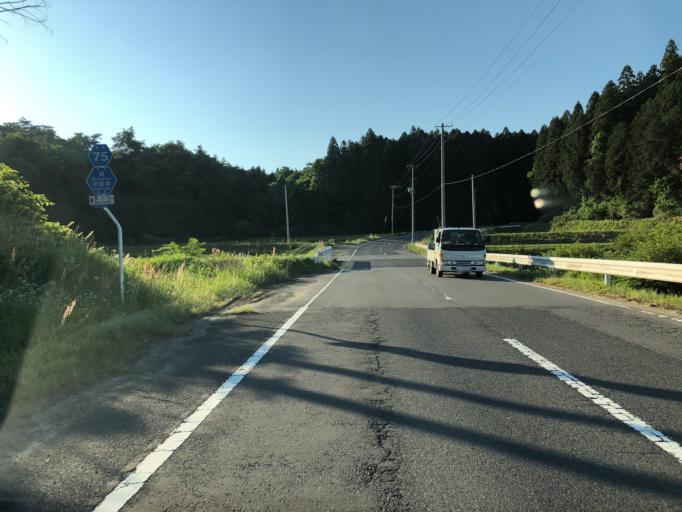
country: JP
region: Fukushima
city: Ishikawa
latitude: 37.0018
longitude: 140.4341
